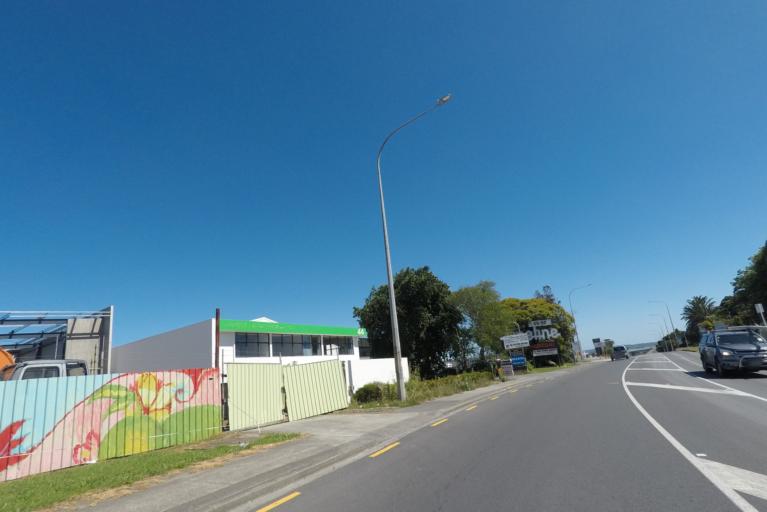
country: NZ
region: Auckland
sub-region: Auckland
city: Rosebank
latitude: -36.8703
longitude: 174.6664
